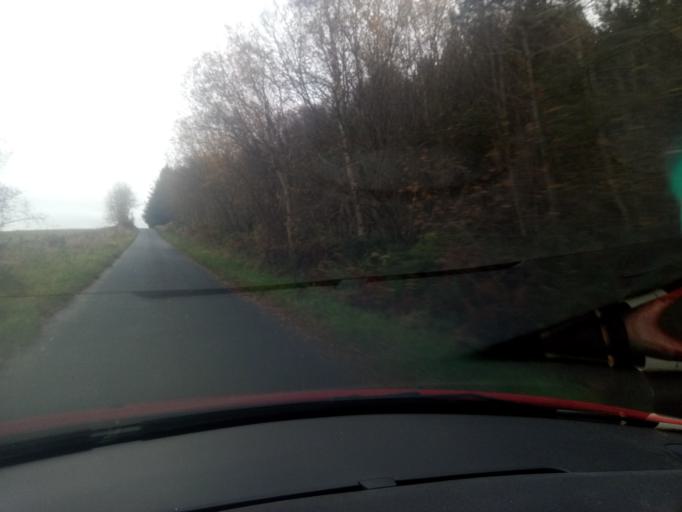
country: GB
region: Scotland
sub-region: The Scottish Borders
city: Jedburgh
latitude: 55.4843
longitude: -2.5870
